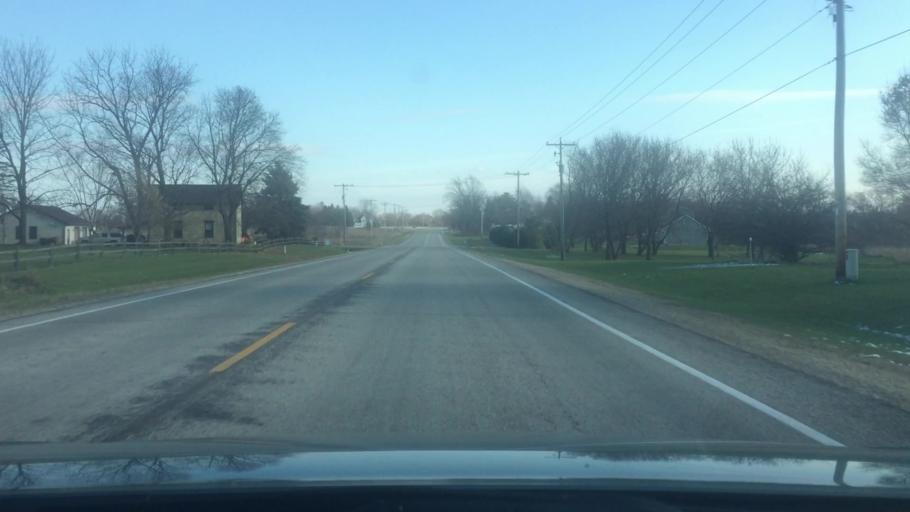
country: US
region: Wisconsin
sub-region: Walworth County
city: Whitewater
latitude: 42.9338
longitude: -88.7275
